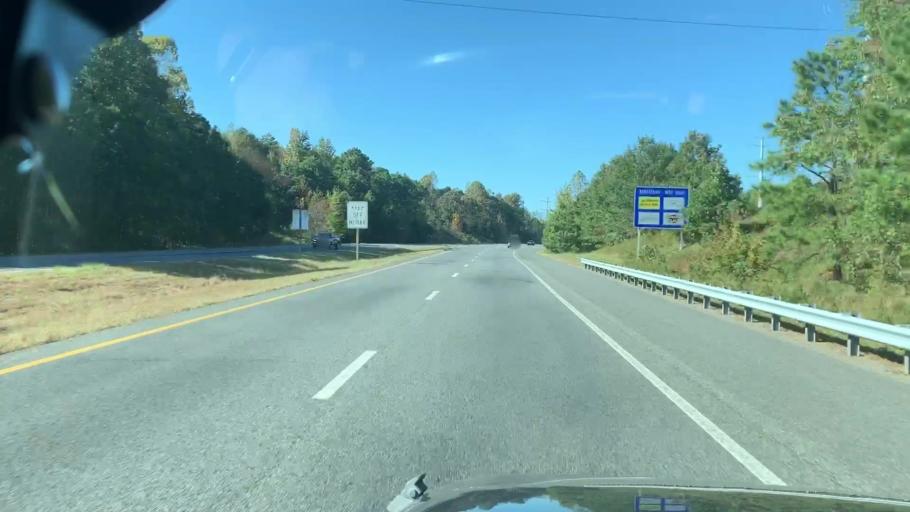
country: US
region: Virginia
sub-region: James City County
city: Williamsburg
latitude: 37.3229
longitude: -76.7531
